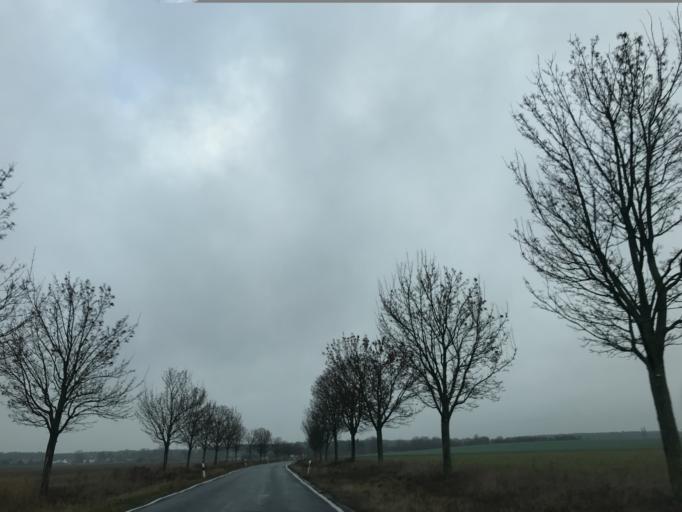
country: DE
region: Brandenburg
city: Brieselang
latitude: 52.6671
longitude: 12.9779
